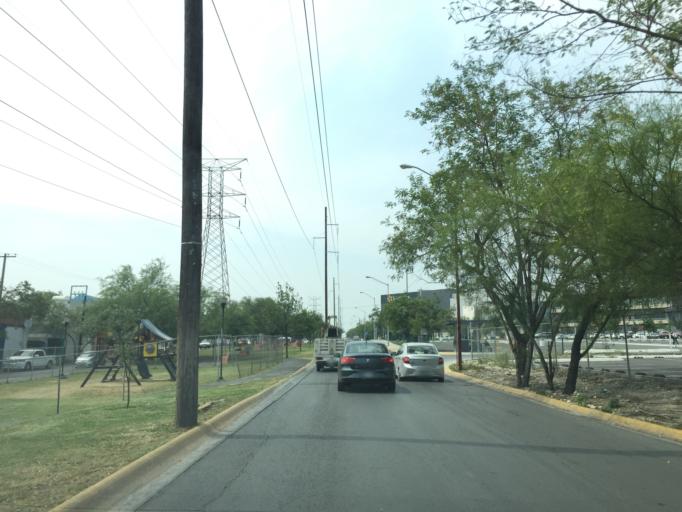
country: MX
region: Nuevo Leon
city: Guadalupe
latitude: 25.7172
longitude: -100.2201
